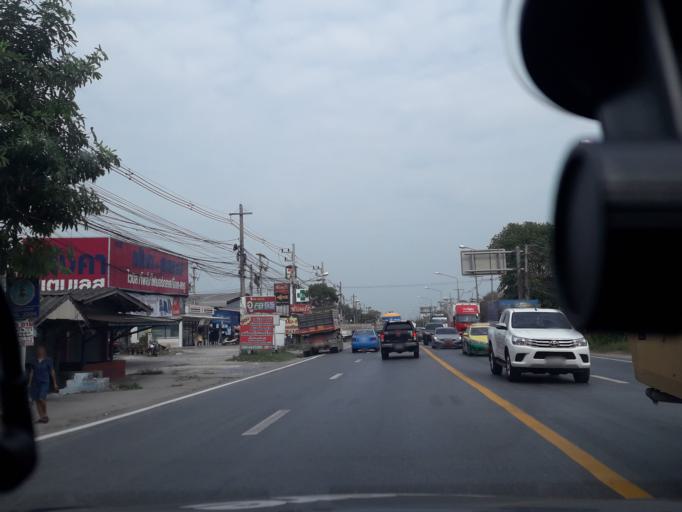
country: TH
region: Pathum Thani
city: Lam Luk Ka
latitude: 13.9357
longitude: 100.7464
